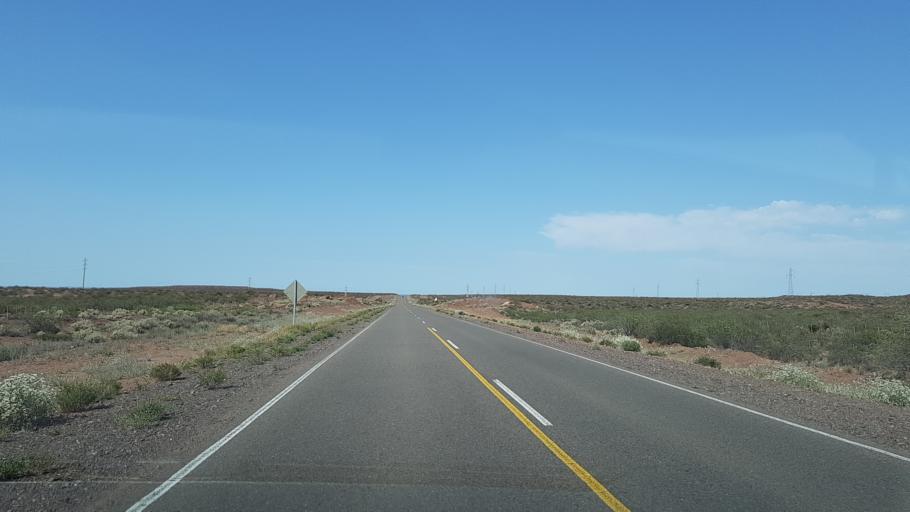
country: AR
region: Neuquen
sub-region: Departamento de Picun Leufu
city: Picun Leufu
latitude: -39.3053
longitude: -68.9249
